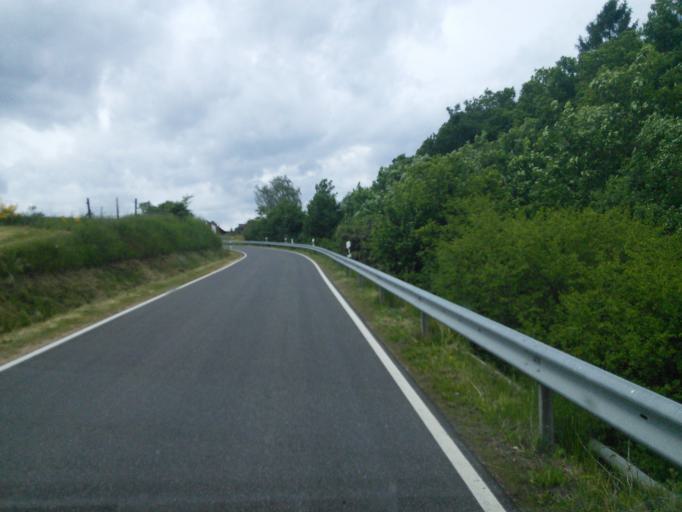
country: DE
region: Rheinland-Pfalz
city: Kirchsahr
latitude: 50.5386
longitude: 6.9083
